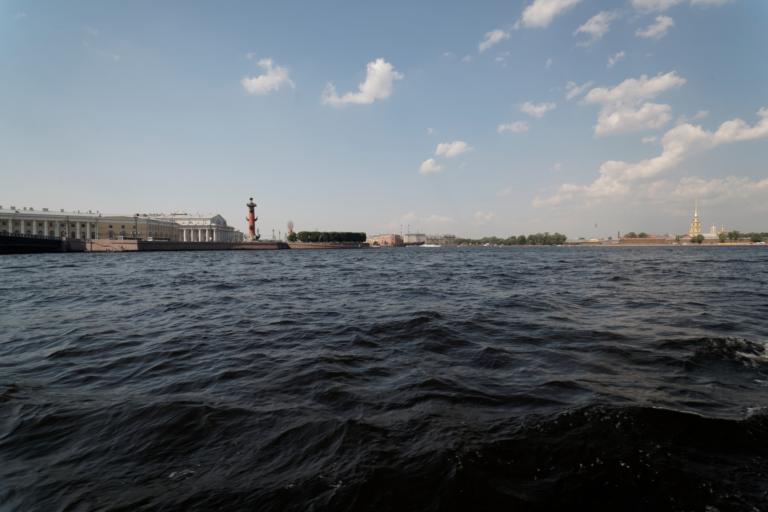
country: RU
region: St.-Petersburg
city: Saint Petersburg
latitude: 59.9416
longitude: 30.3110
